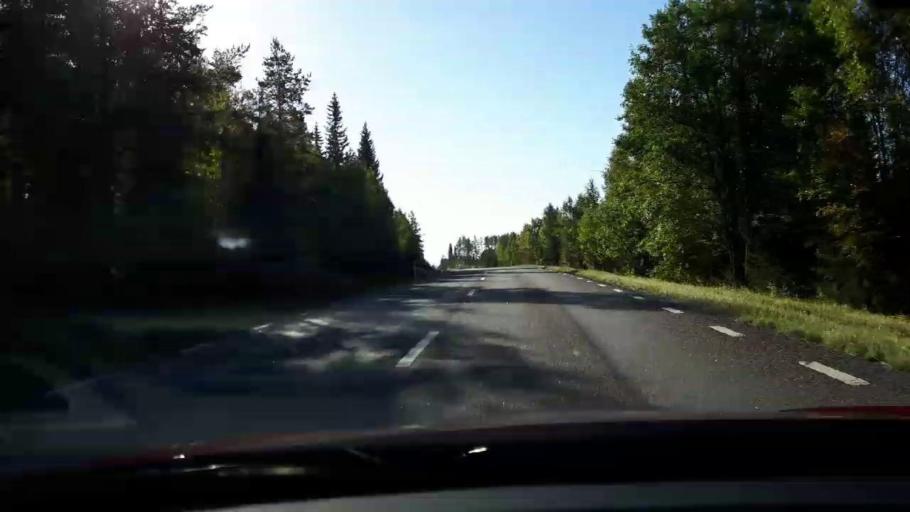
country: SE
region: Jaemtland
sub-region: OEstersunds Kommun
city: Brunflo
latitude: 62.9657
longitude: 15.0230
